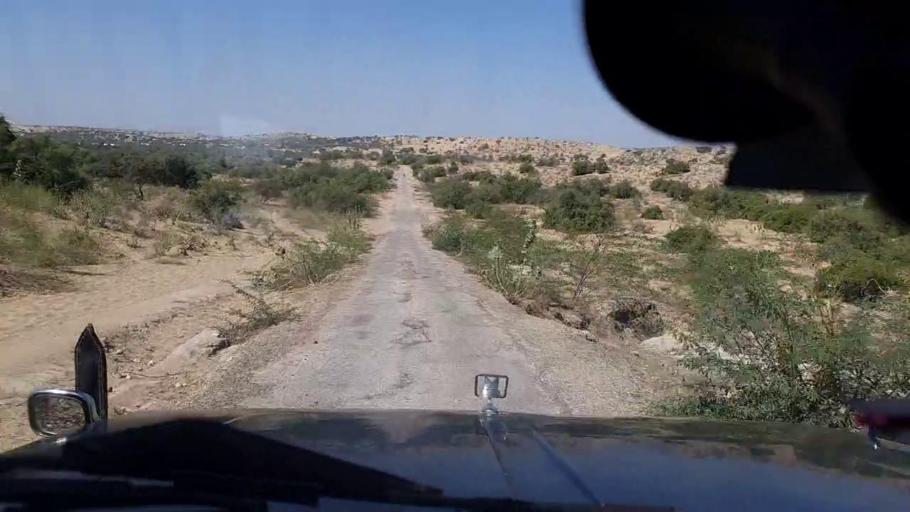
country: PK
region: Sindh
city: Mithi
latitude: 24.6134
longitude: 69.6969
